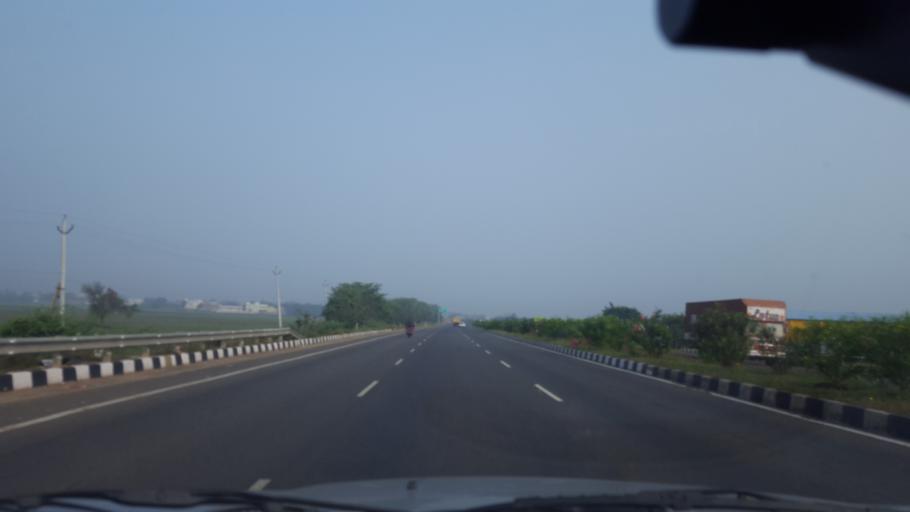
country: IN
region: Andhra Pradesh
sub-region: Prakasam
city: Ongole
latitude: 15.3815
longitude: 80.0409
